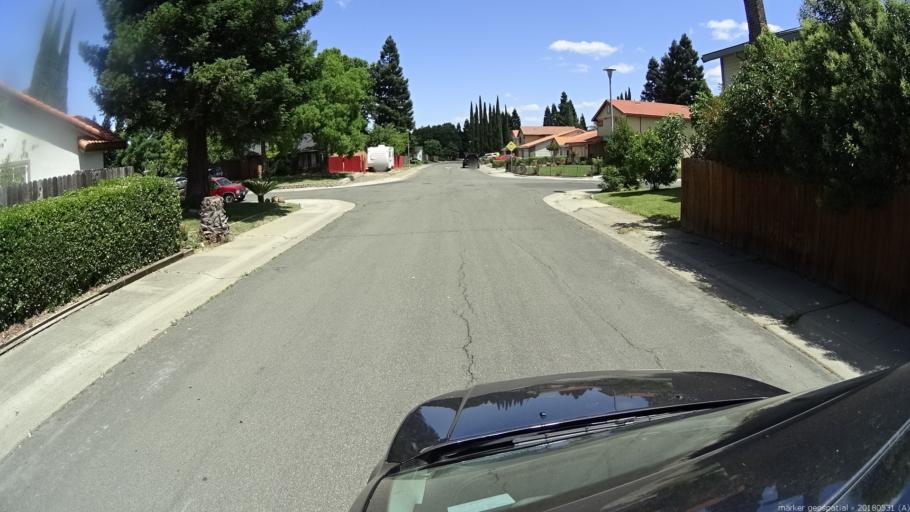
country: US
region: California
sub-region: Yolo County
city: West Sacramento
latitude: 38.6238
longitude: -121.5143
